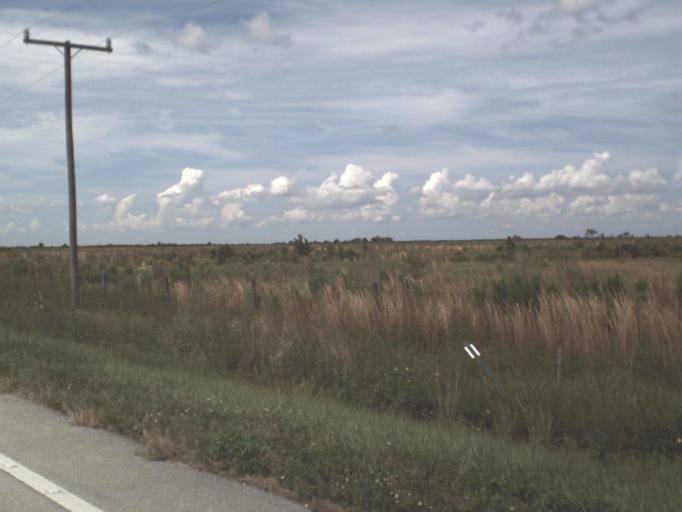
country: US
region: Florida
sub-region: Highlands County
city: Placid Lakes
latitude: 27.2092
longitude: -81.5518
